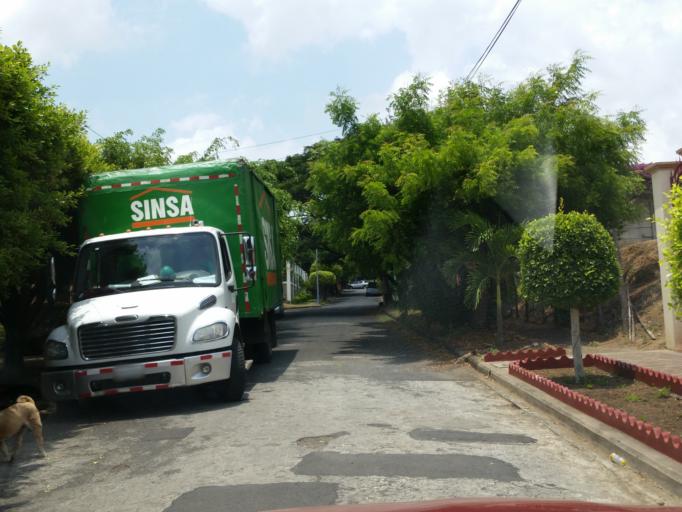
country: NI
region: Managua
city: Managua
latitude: 12.0958
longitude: -86.2455
